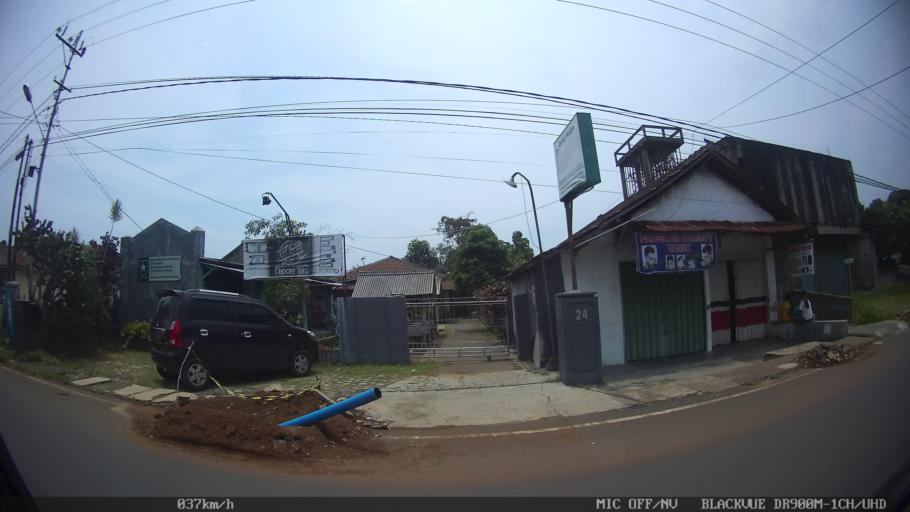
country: ID
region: Lampung
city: Bandarlampung
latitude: -5.4125
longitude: 105.2739
